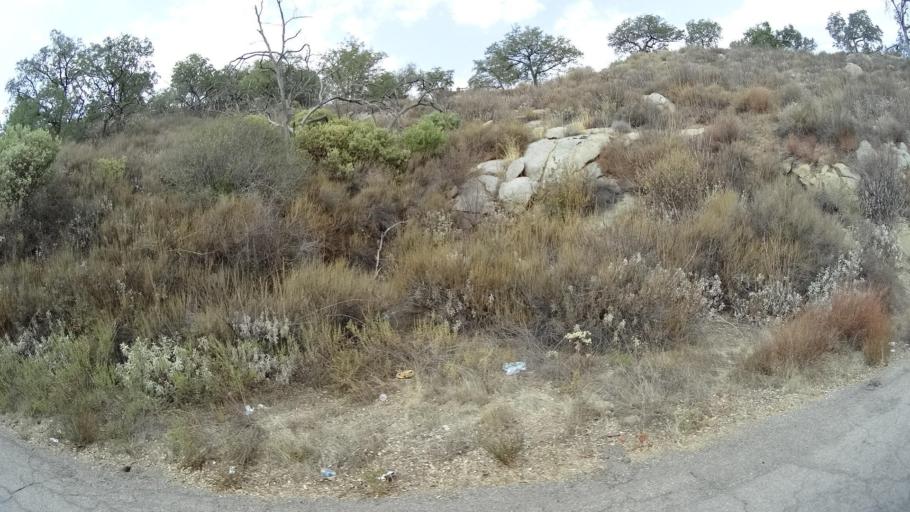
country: US
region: California
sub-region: San Diego County
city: San Diego Country Estates
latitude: 33.1019
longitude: -116.7896
